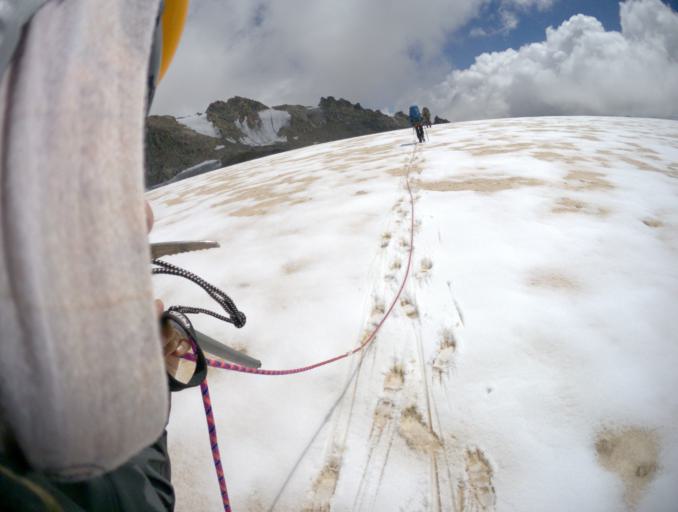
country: RU
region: Kabardino-Balkariya
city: Terskol
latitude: 43.3351
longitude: 42.5137
